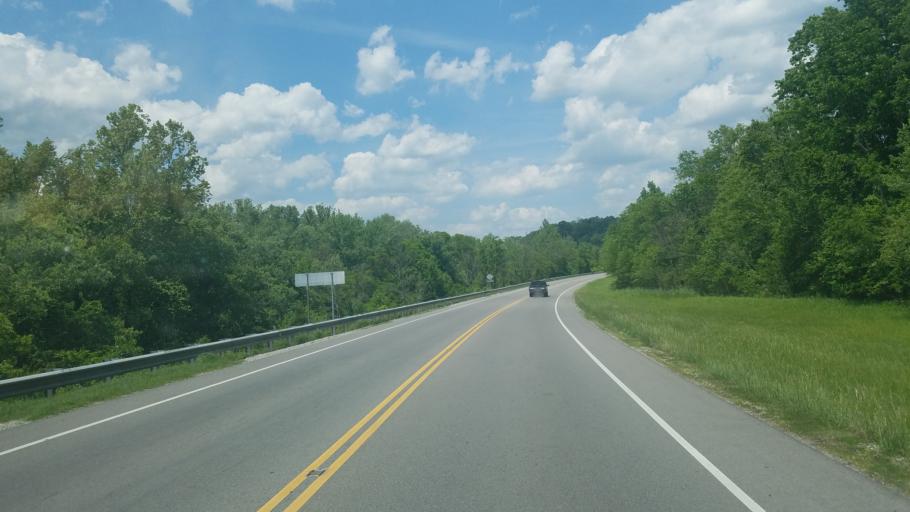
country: US
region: Ohio
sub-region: Meigs County
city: Middleport
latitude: 38.9984
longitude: -82.0764
